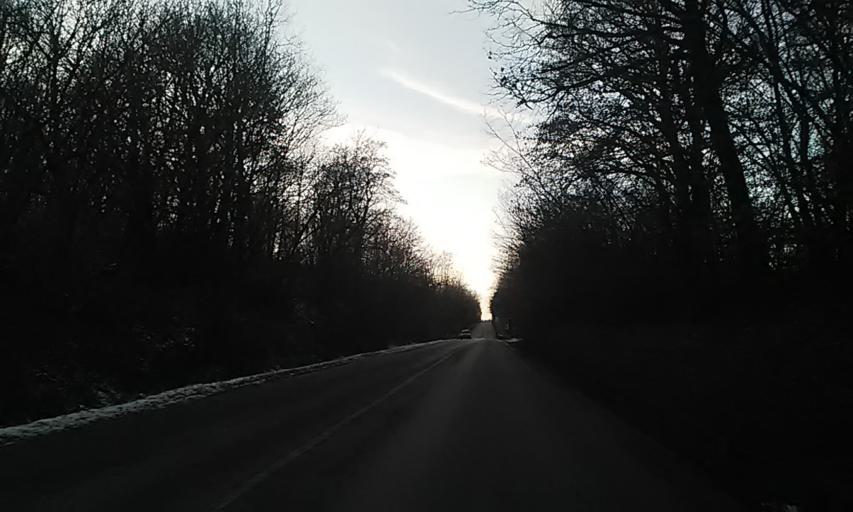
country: IT
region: Piedmont
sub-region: Provincia di Biella
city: Masserano
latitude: 45.5660
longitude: 8.2250
